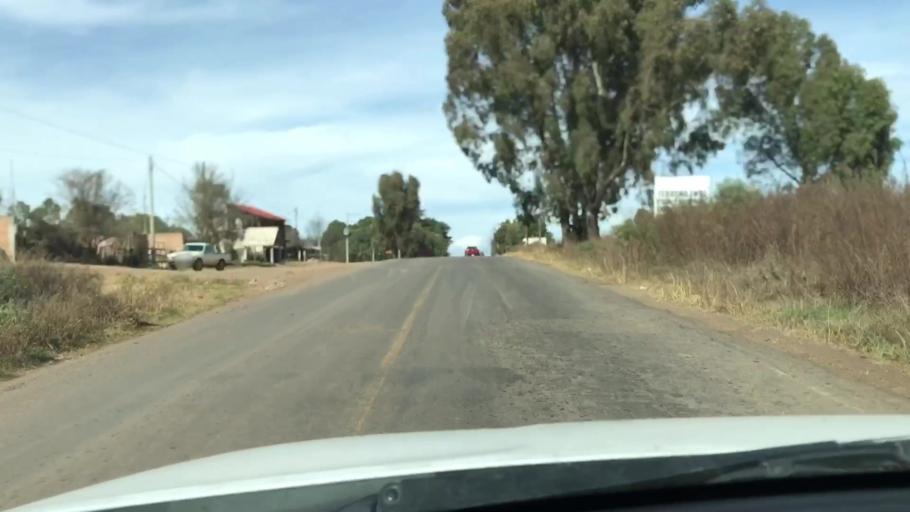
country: MX
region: Jalisco
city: Chiquilistlan
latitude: 20.1222
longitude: -103.7237
